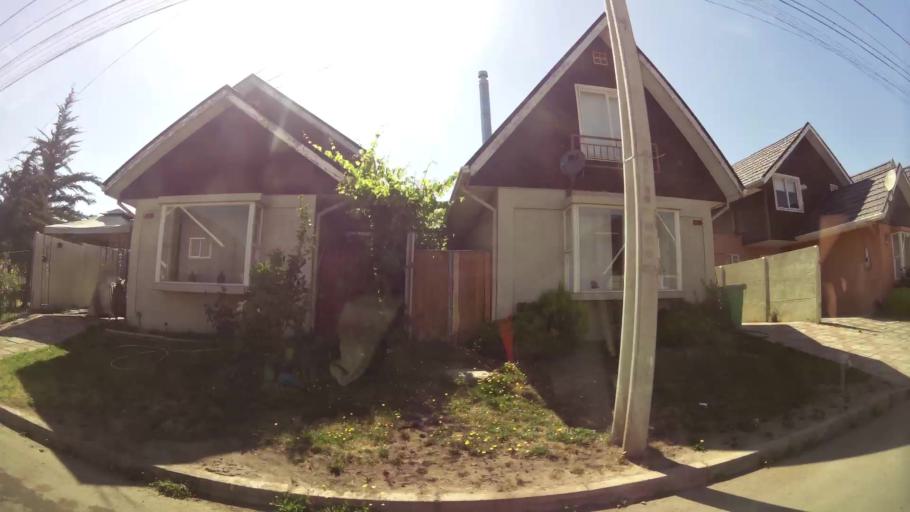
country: CL
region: Santiago Metropolitan
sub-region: Provincia de Maipo
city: San Bernardo
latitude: -33.6177
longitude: -70.6830
